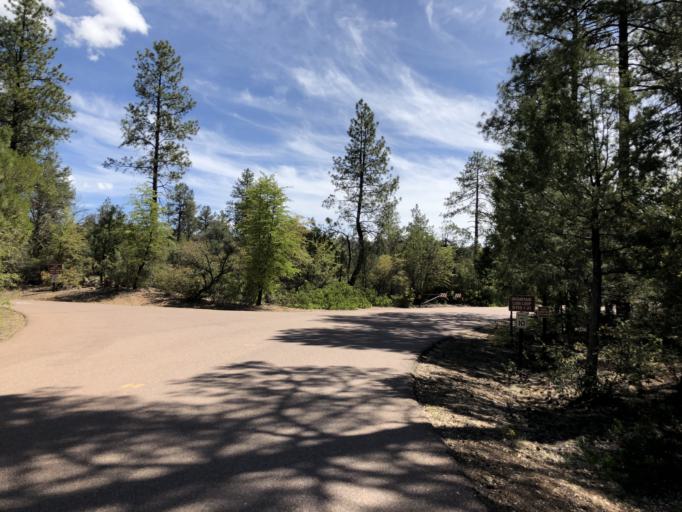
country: US
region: Arizona
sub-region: Gila County
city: Payson
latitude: 34.2726
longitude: -111.3184
